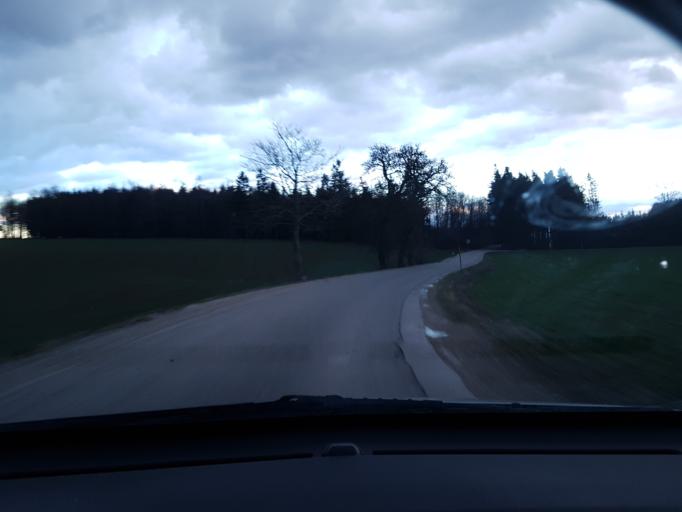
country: AT
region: Upper Austria
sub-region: Politischer Bezirk Linz-Land
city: Ansfelden
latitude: 48.1539
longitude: 14.3108
